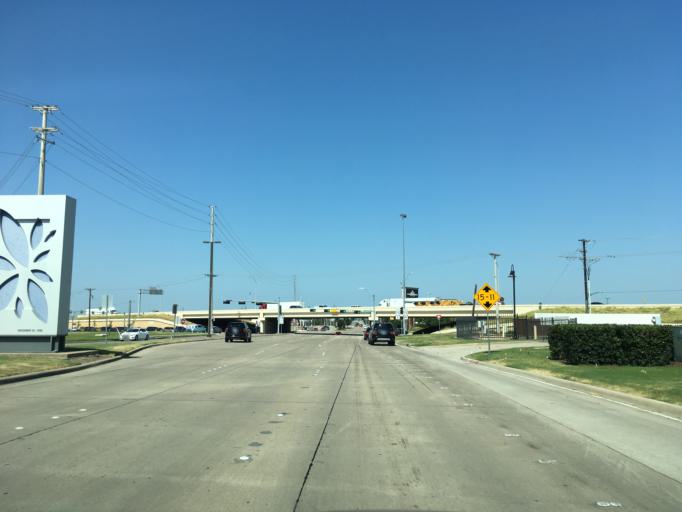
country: US
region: Texas
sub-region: Collin County
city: Allen
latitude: 33.1300
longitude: -96.6578
